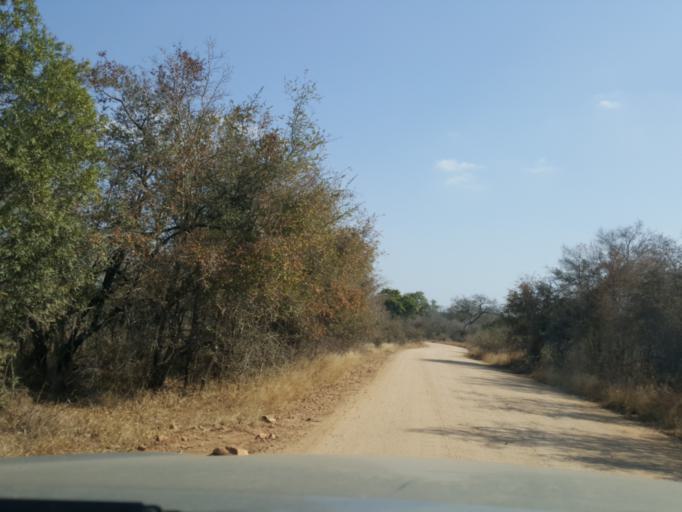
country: ZA
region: Mpumalanga
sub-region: Ehlanzeni District
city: Komatipoort
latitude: -25.2889
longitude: 31.7708
